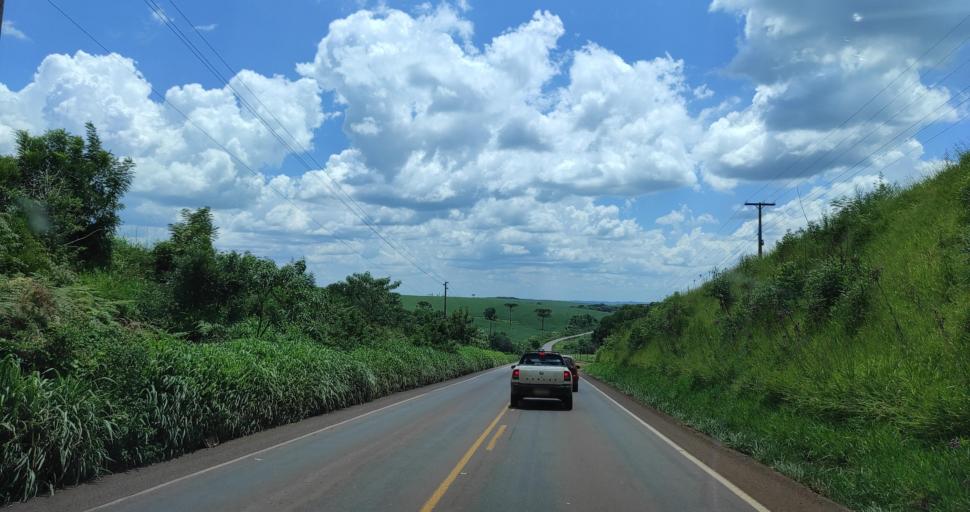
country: BR
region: Santa Catarina
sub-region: Xanxere
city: Xanxere
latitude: -26.8292
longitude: -52.4148
